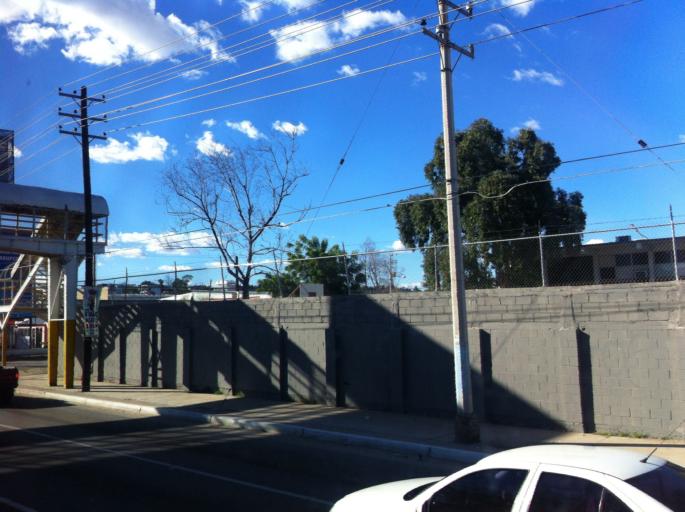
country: MX
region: Sonora
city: Hermosillo
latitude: 29.1018
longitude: -110.9153
